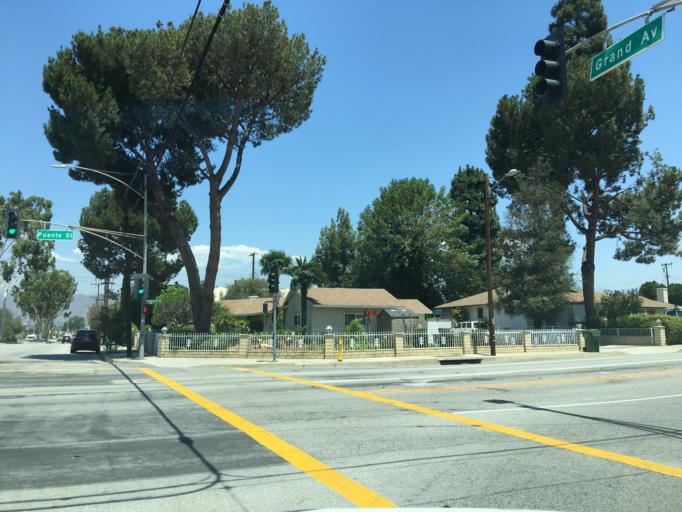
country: US
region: California
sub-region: Los Angeles County
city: Covina
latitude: 34.0824
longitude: -117.8724
